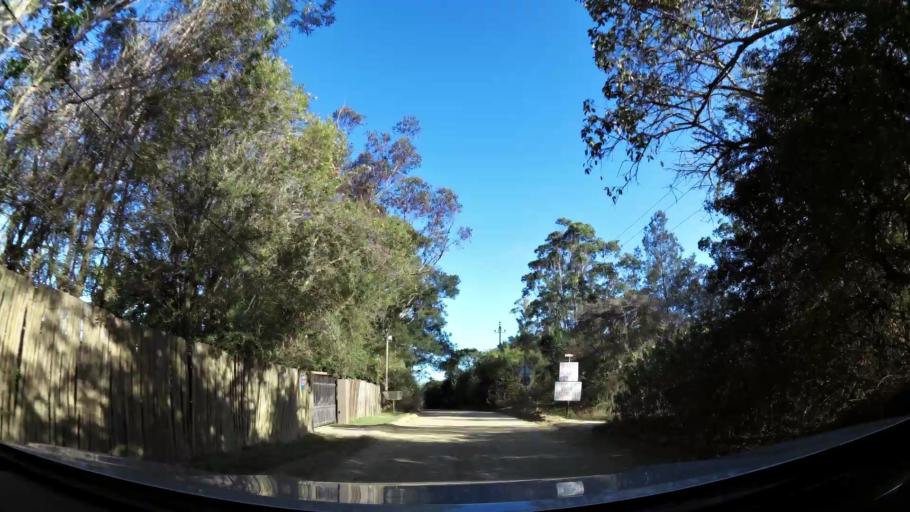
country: ZA
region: Western Cape
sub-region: Eden District Municipality
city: George
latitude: -33.9844
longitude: 22.5683
